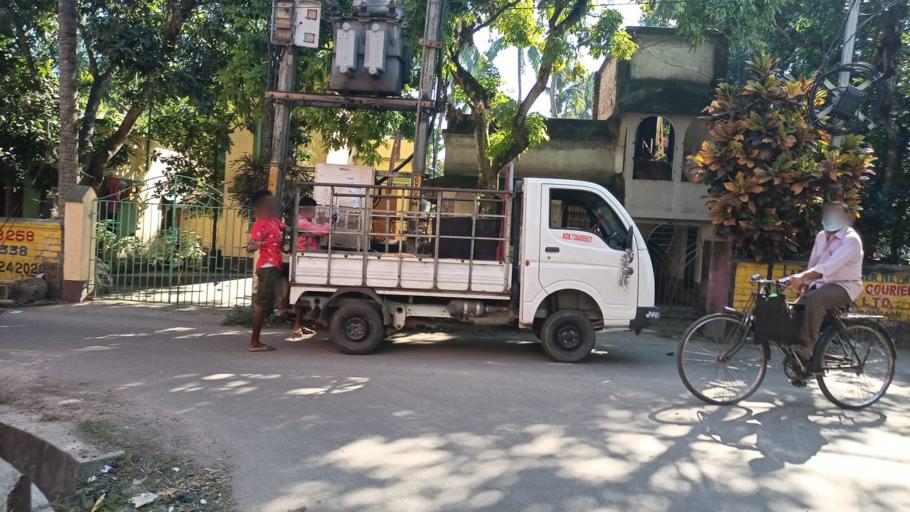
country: IN
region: West Bengal
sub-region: North 24 Parganas
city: Bangaon
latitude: 23.0506
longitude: 88.8242
